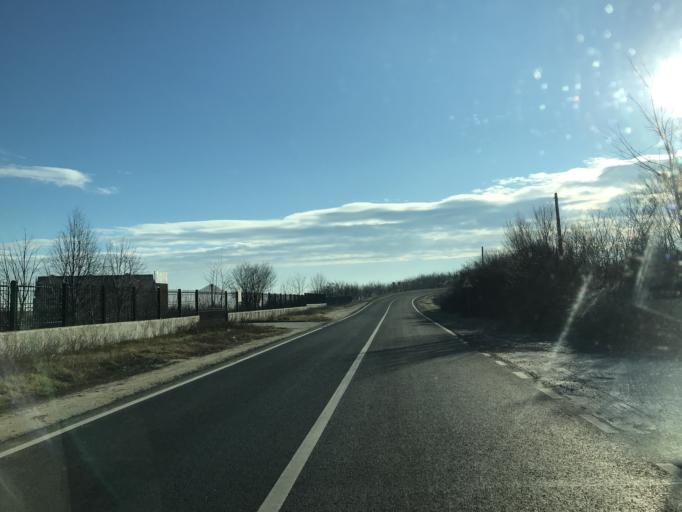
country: RO
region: Olt
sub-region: Comuna Ganeasa
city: Ganeasa
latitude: 44.3963
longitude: 24.2791
